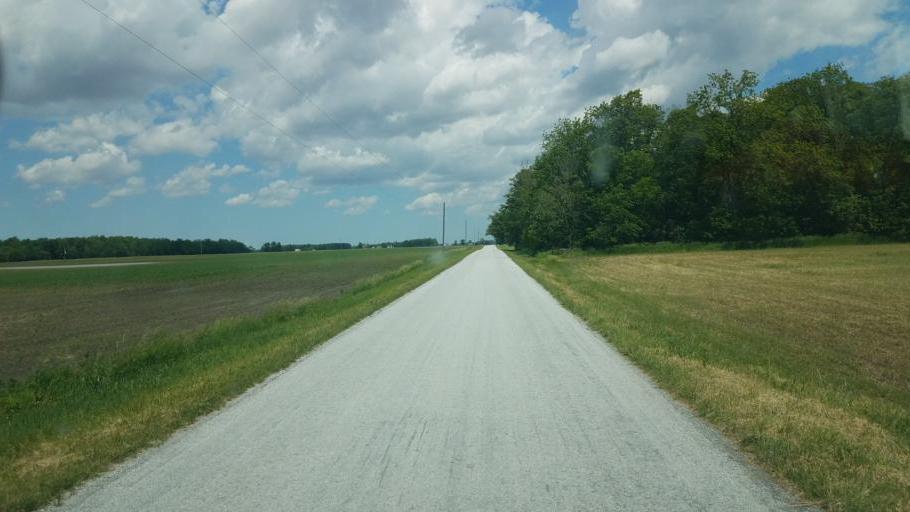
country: US
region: Ohio
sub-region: Hardin County
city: Kenton
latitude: 40.6684
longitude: -83.4772
